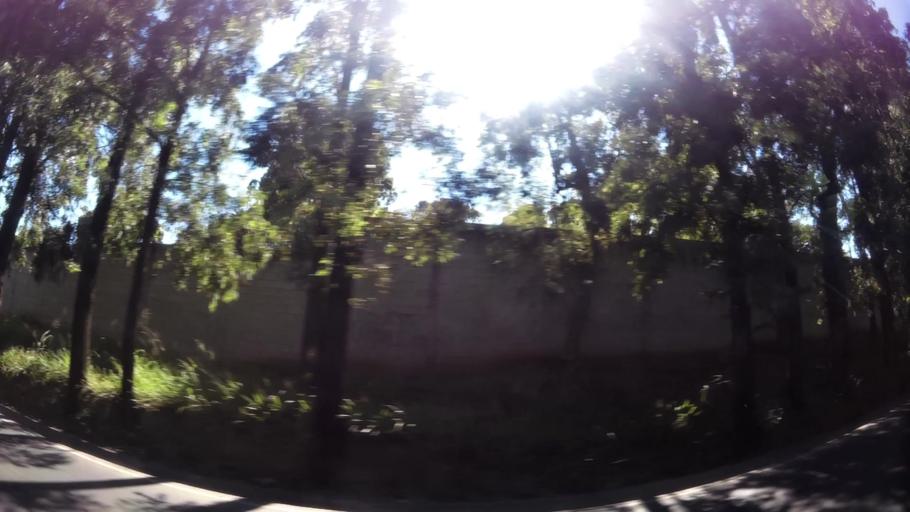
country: GT
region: Guatemala
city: Villa Nueva
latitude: 14.5403
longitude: -90.6108
